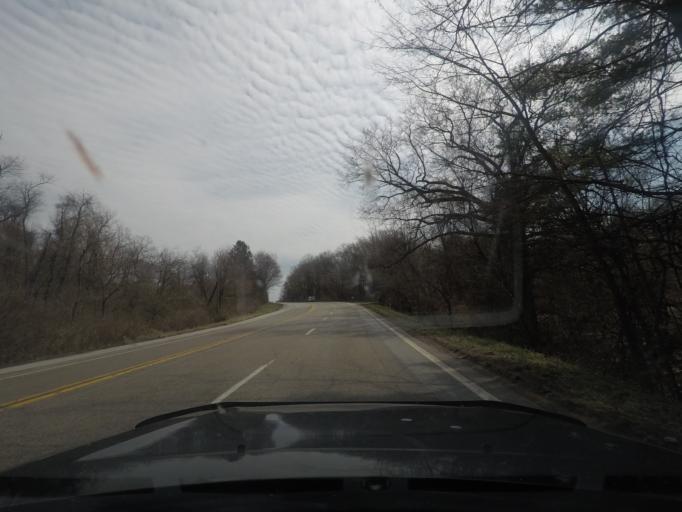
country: US
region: Indiana
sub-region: LaPorte County
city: LaPorte
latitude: 41.6622
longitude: -86.7710
